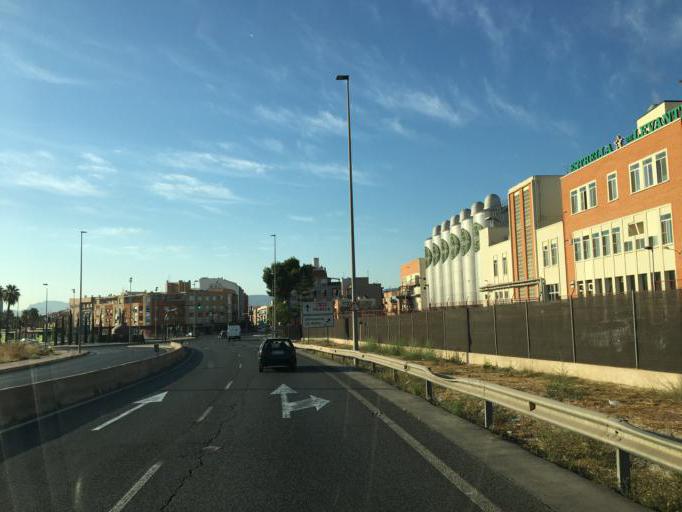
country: ES
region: Murcia
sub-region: Murcia
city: Murcia
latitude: 38.0148
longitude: -1.1576
